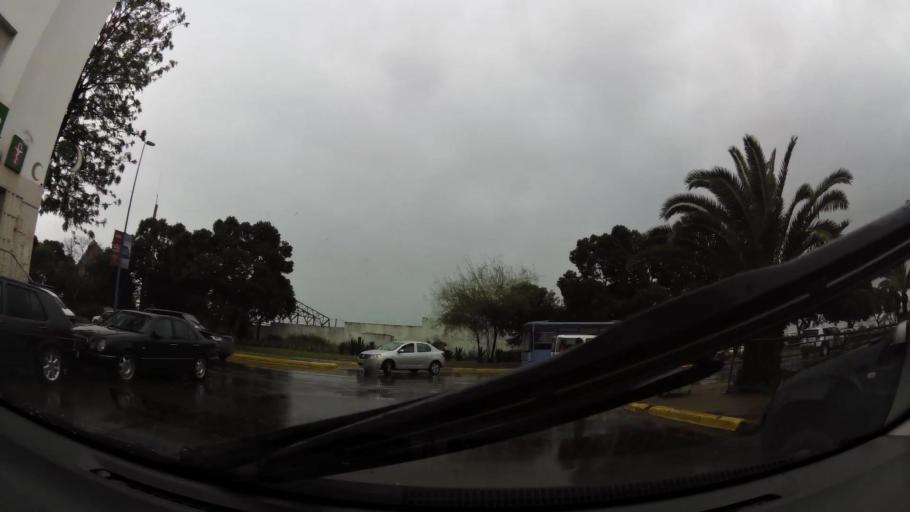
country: MA
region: Grand Casablanca
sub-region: Casablanca
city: Casablanca
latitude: 33.5568
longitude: -7.6673
